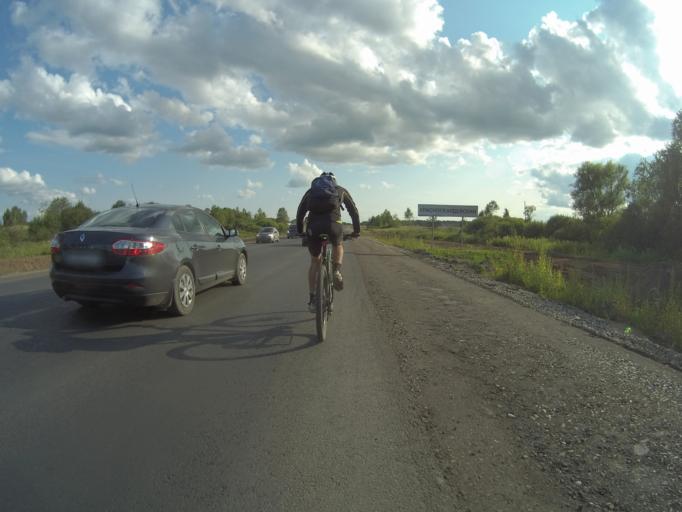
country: RU
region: Vladimir
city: Kideksha
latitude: 56.5100
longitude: 40.5469
